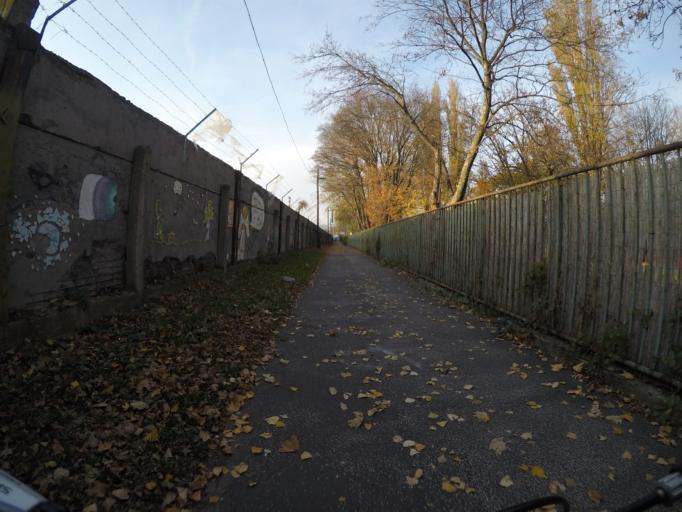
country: SK
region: Bratislavsky
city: Bratislava
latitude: 48.1725
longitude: 17.1591
